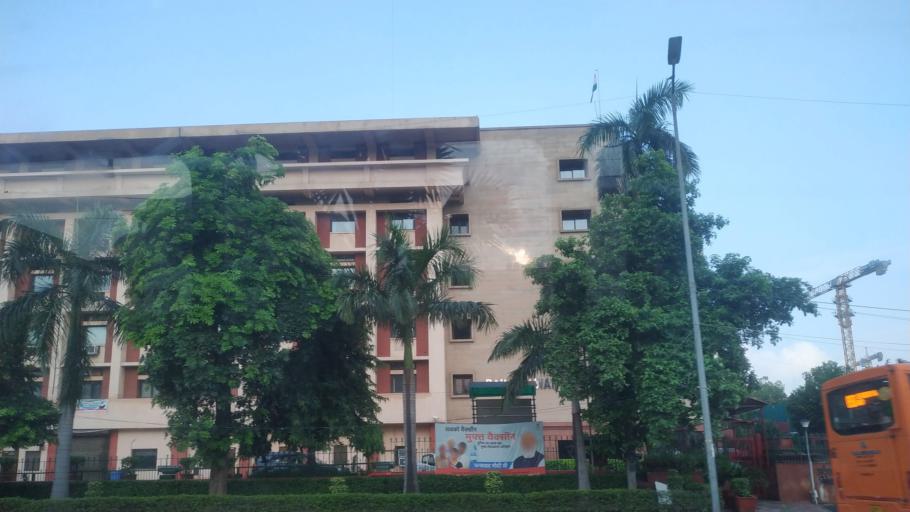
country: IN
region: NCT
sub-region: New Delhi
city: New Delhi
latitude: 28.6161
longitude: 77.2123
